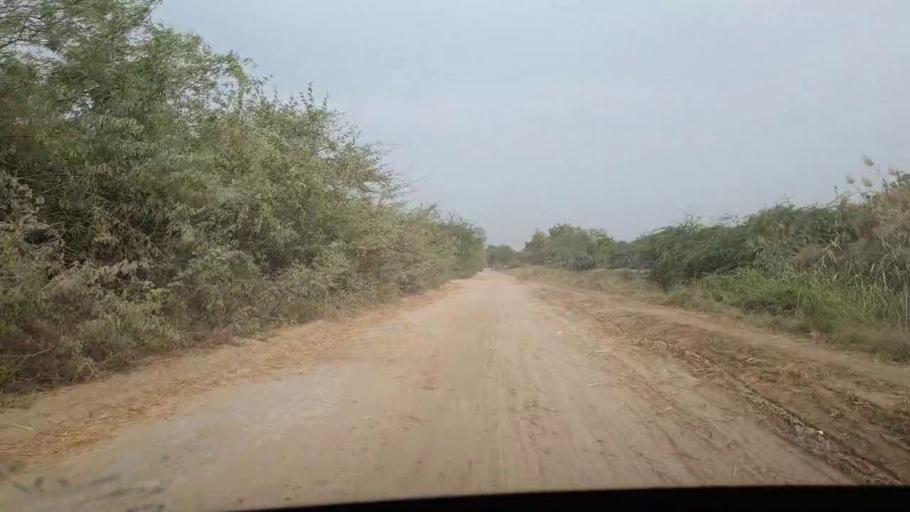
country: PK
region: Sindh
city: Chuhar Jamali
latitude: 24.3946
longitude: 67.9737
